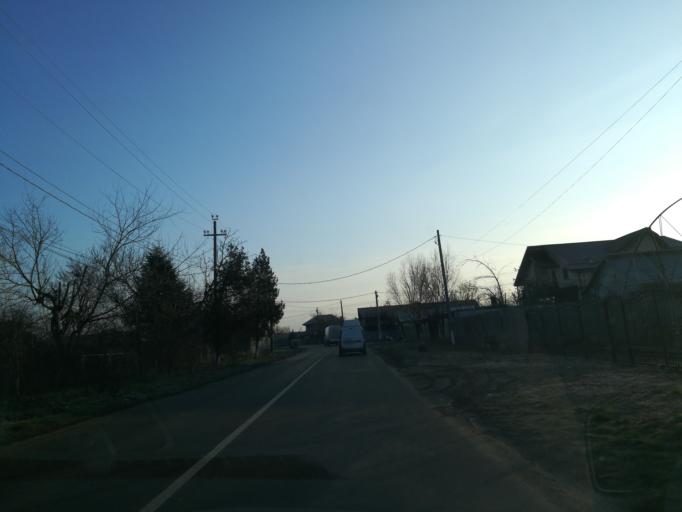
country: RO
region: Ilfov
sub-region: Comuna Moara Vlasiei
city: Caciulati
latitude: 44.6278
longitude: 26.1579
